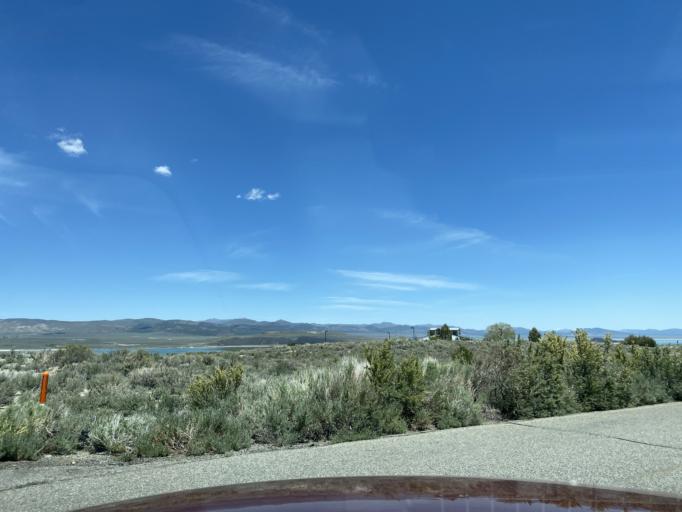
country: US
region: California
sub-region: Mono County
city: Bridgeport
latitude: 37.9647
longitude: -119.1218
